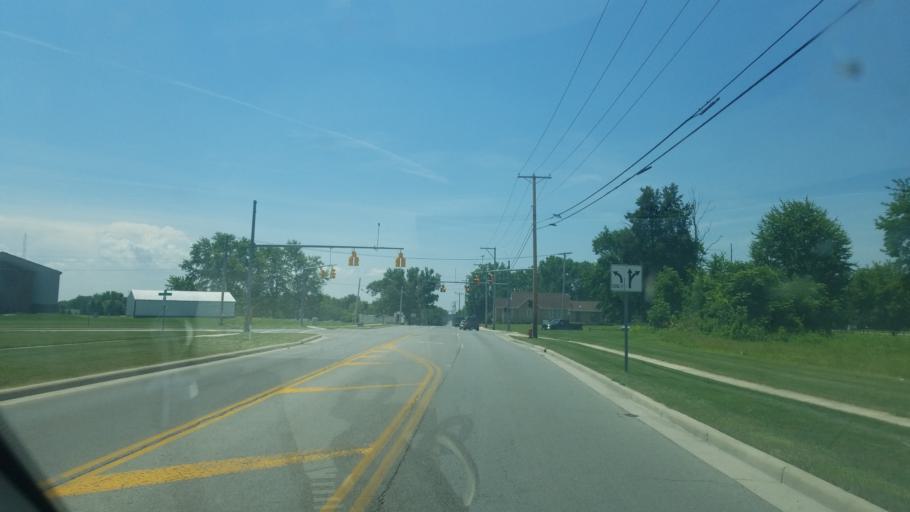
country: US
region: Ohio
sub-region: Hancock County
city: Findlay
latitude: 41.0663
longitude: -83.6315
